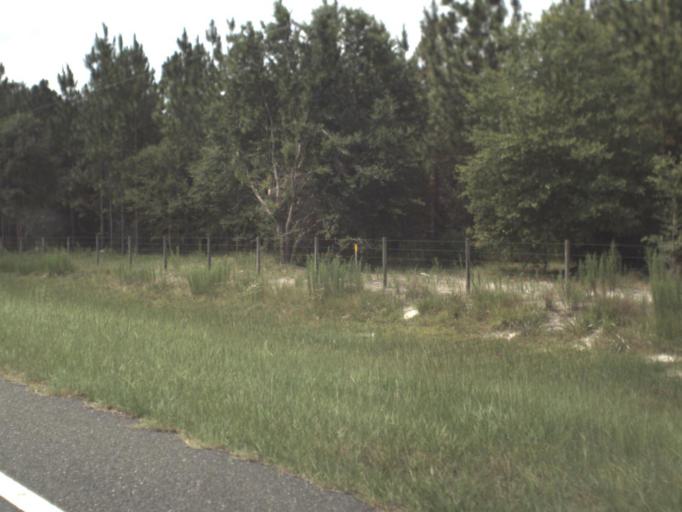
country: US
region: Florida
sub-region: Levy County
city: Chiefland
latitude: 29.4206
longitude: -82.8257
